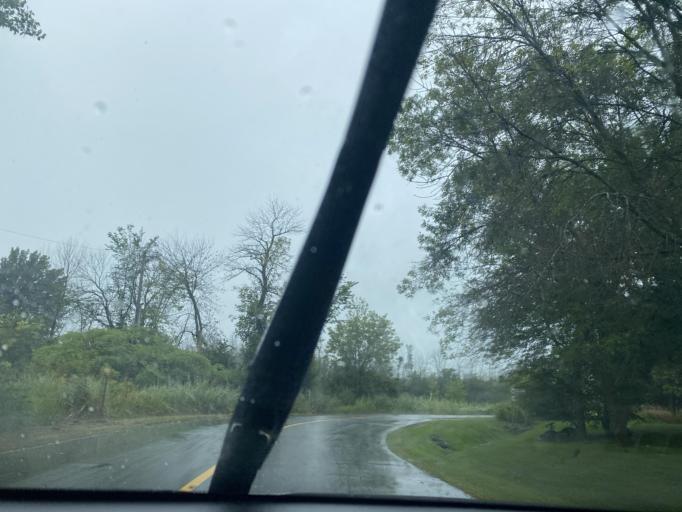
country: CA
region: Quebec
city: Baie-D'Urfe
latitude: 45.4617
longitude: -73.9209
